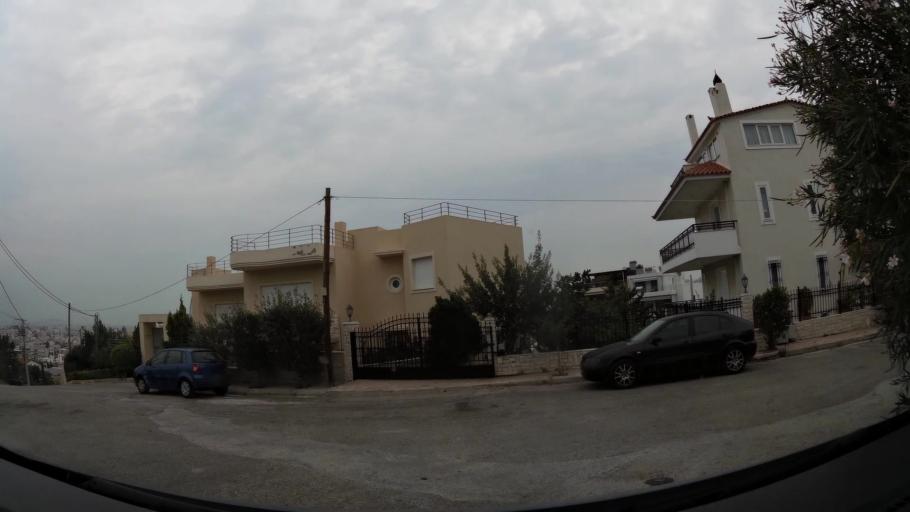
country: GR
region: Attica
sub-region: Nomarchia Athinas
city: Alimos
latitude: 37.9123
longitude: 23.7266
